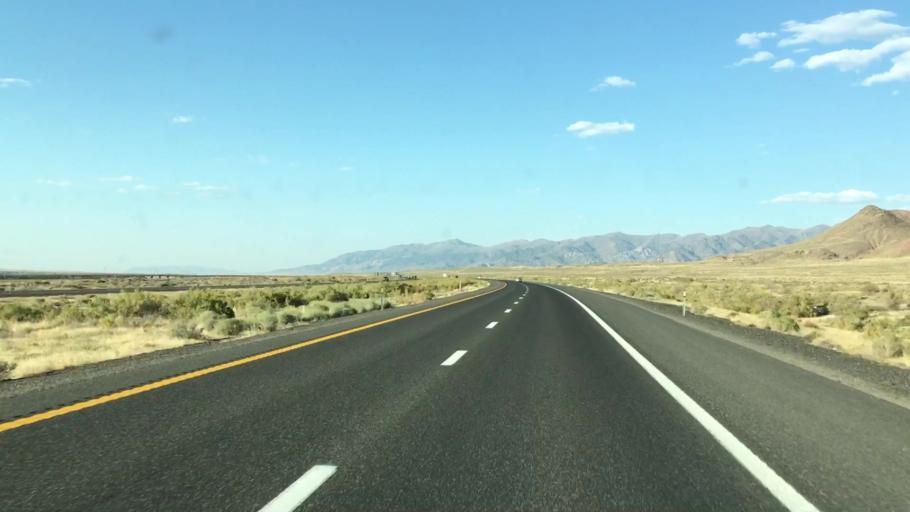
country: US
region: Nevada
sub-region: Pershing County
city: Lovelock
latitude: 40.2538
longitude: -118.3776
